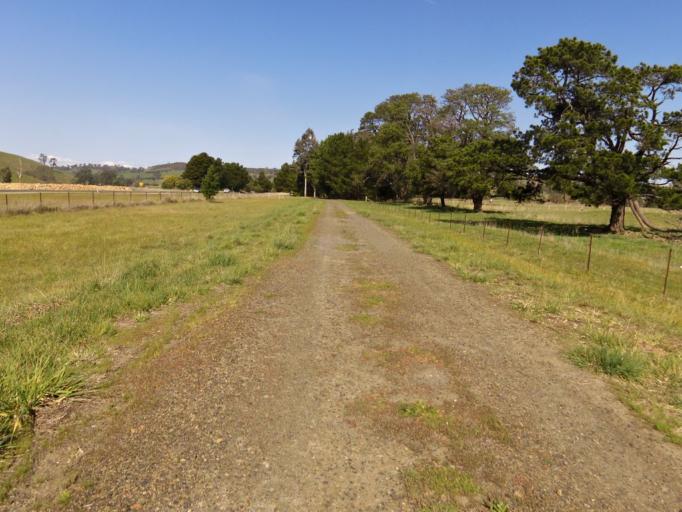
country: AU
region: Victoria
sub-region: Murrindindi
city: Alexandra
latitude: -37.0072
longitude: 145.7511
